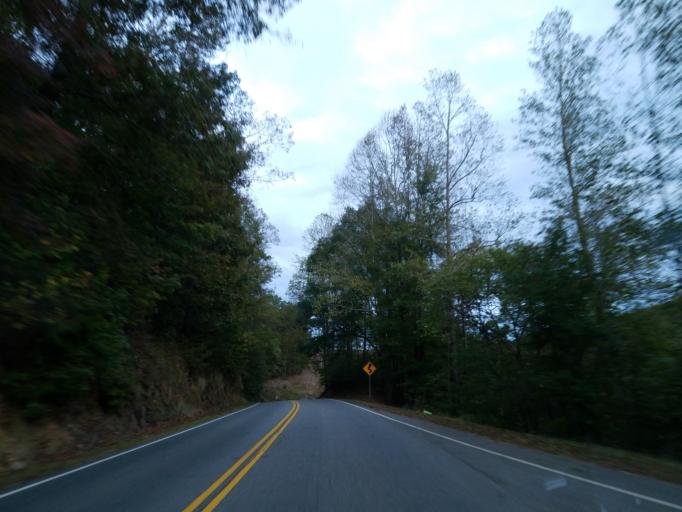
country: US
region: Georgia
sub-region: Dawson County
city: Dawsonville
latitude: 34.3760
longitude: -84.1189
